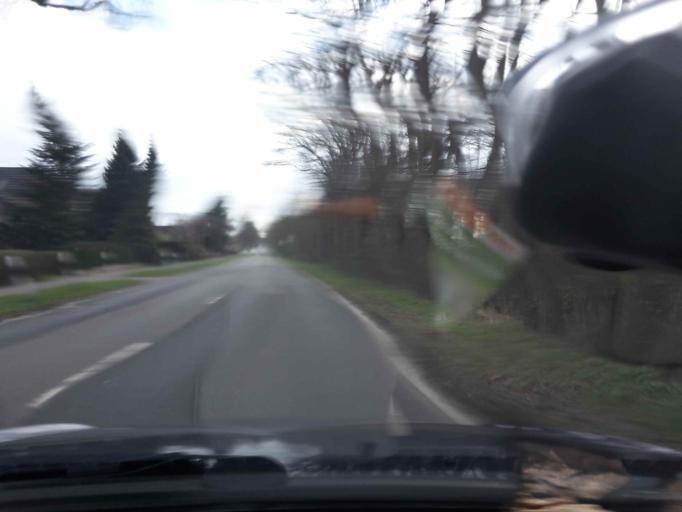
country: DE
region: Lower Saxony
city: Buchholz in der Nordheide
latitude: 53.3233
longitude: 9.8853
